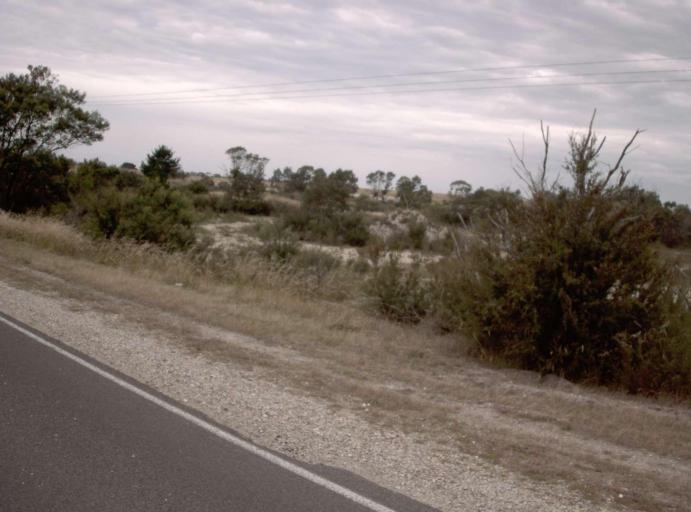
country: AU
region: Victoria
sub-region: Wellington
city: Sale
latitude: -38.1880
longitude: 147.2754
